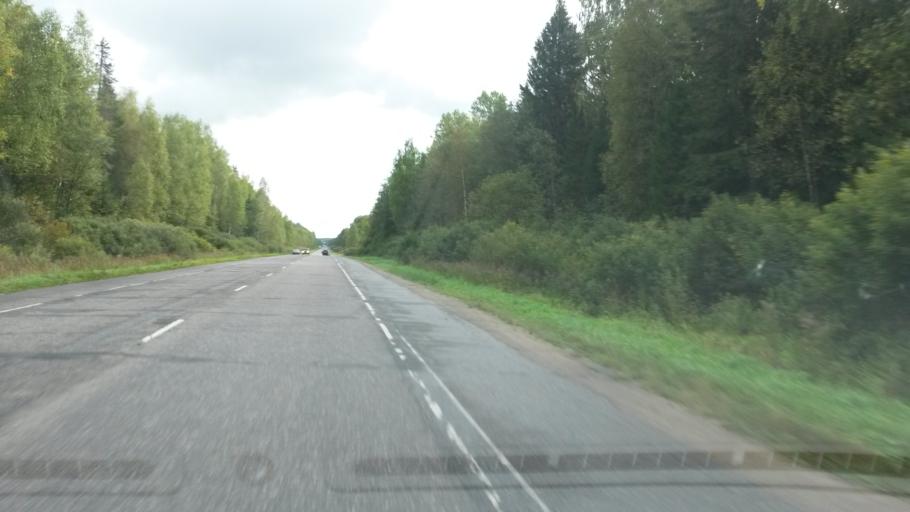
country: RU
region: Ivanovo
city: Kaminskiy
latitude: 57.0852
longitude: 41.5928
